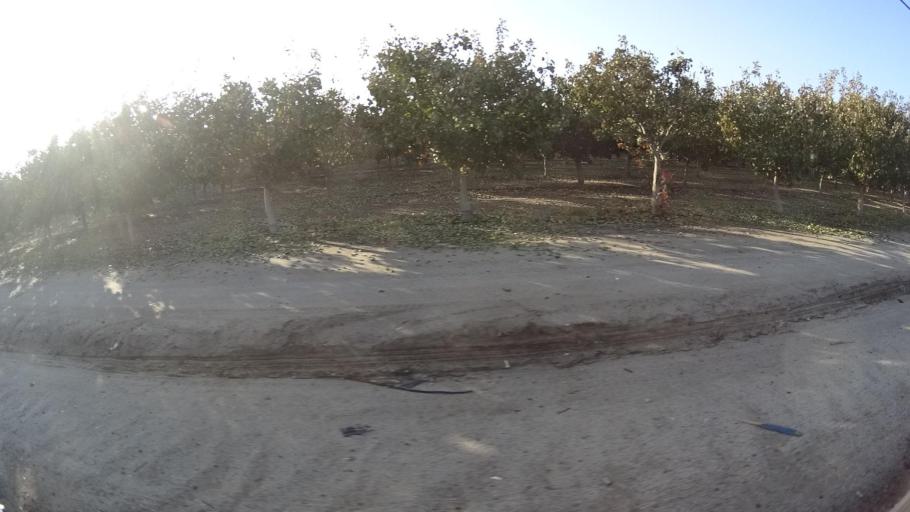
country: US
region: California
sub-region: Tulare County
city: Richgrove
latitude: 35.7906
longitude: -119.1513
